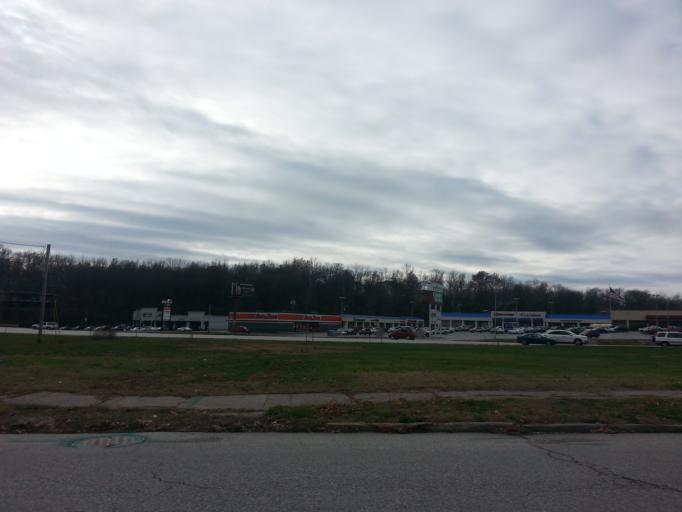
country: US
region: Missouri
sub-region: Marion County
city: Hannibal
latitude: 39.7121
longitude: -91.3907
